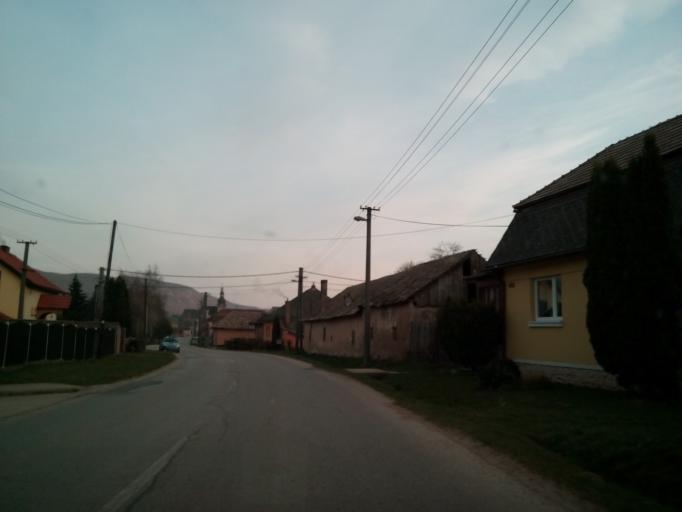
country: SK
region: Kosicky
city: Dobsina
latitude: 48.6633
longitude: 20.3610
